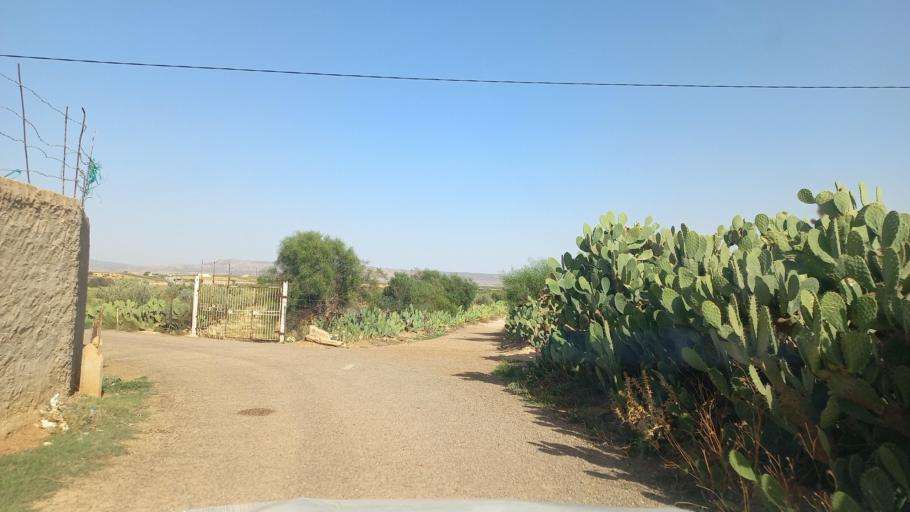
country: TN
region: Al Qasrayn
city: Kasserine
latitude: 35.3160
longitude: 9.0130
